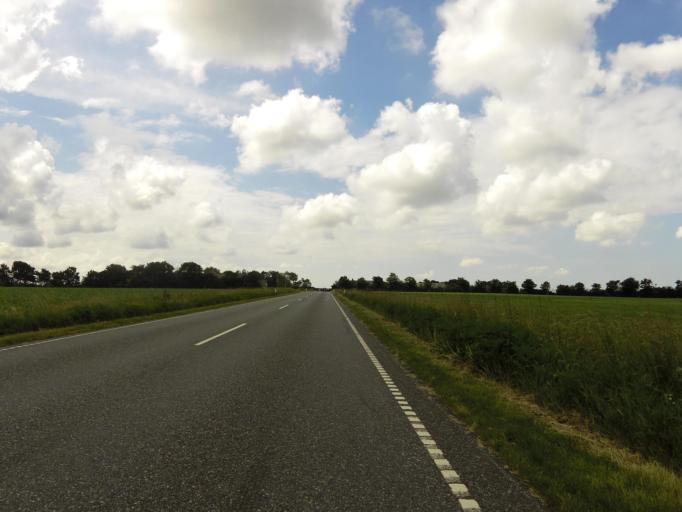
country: DK
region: South Denmark
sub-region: Tonder Kommune
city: Sherrebek
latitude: 55.2211
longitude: 8.9067
